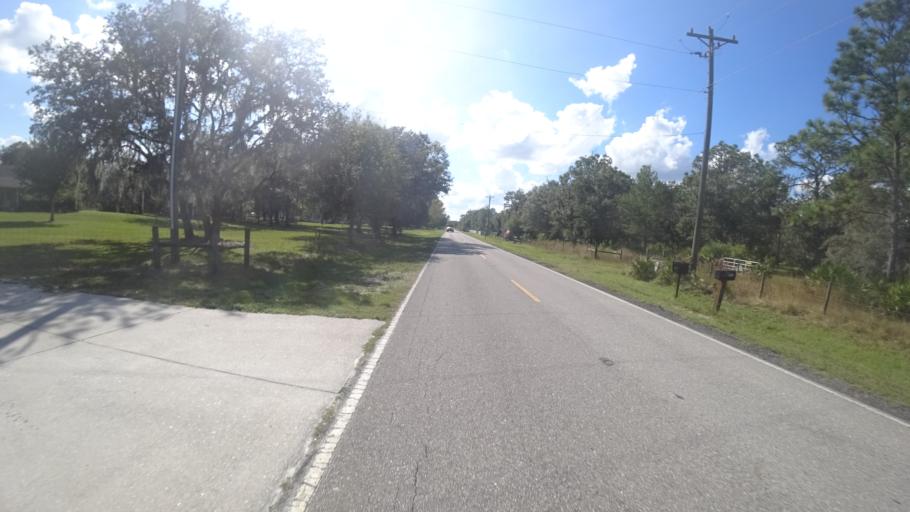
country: US
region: Florida
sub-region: Hillsborough County
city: Wimauma
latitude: 27.4430
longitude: -82.1205
